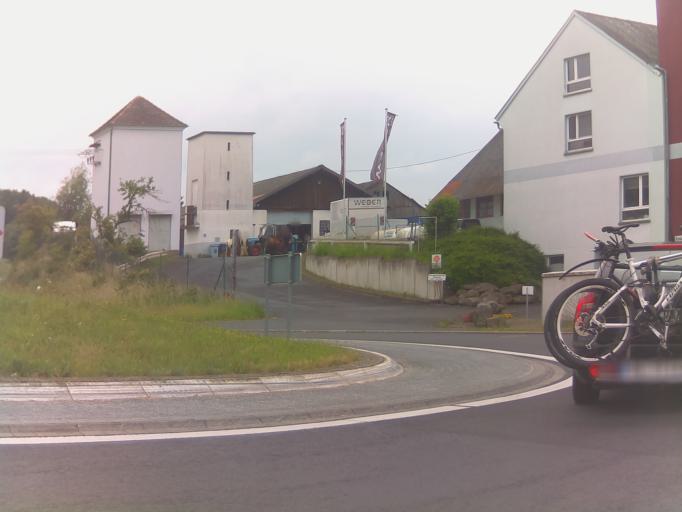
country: DE
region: Bavaria
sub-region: Regierungsbezirk Unterfranken
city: Motten
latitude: 50.4622
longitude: 9.7729
